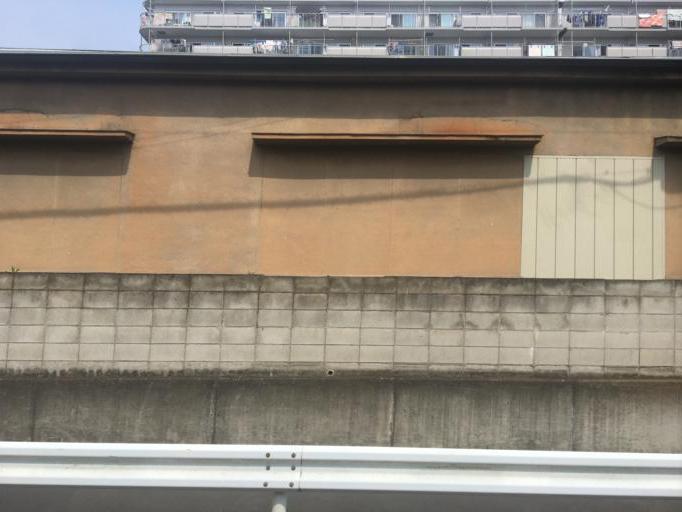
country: JP
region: Saitama
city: Asaka
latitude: 35.7963
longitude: 139.5663
